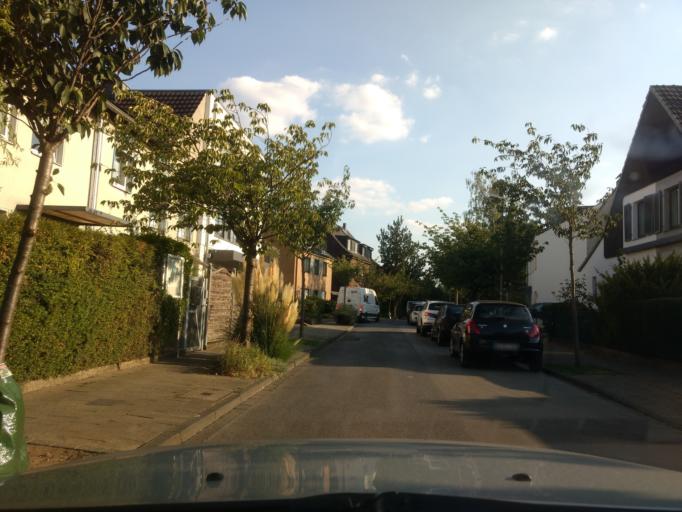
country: DE
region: North Rhine-Westphalia
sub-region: Regierungsbezirk Dusseldorf
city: Meerbusch
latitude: 51.2474
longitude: 6.7018
